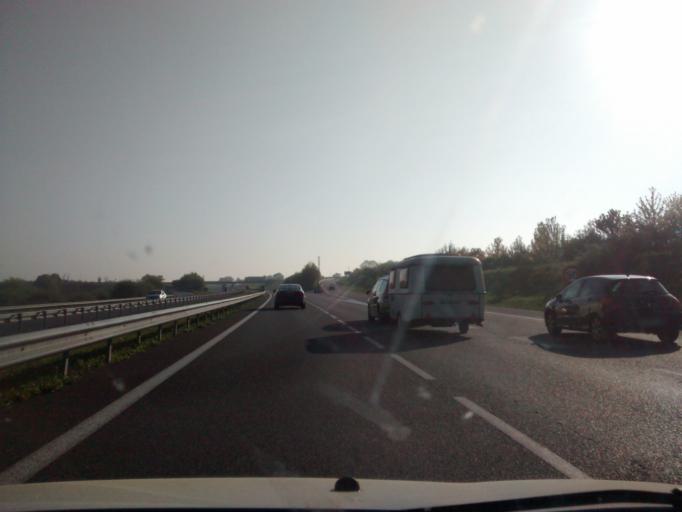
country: FR
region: Brittany
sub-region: Departement d'Ille-et-Vilaine
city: Liffre
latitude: 48.2190
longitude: -1.5047
